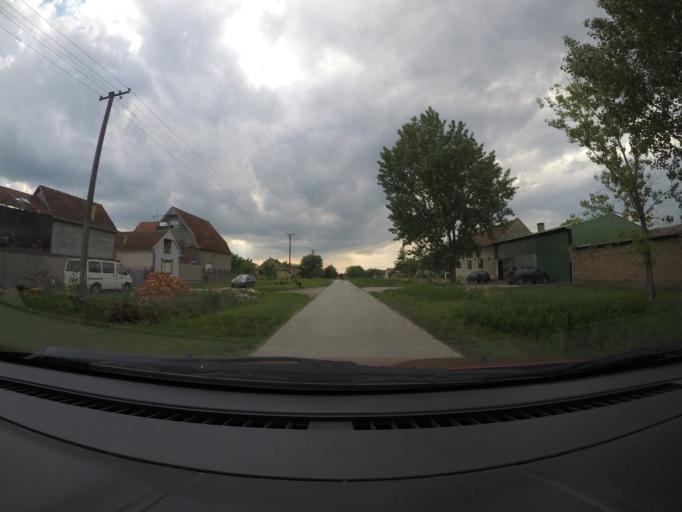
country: RS
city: Uzdin
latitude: 45.2044
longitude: 20.6177
